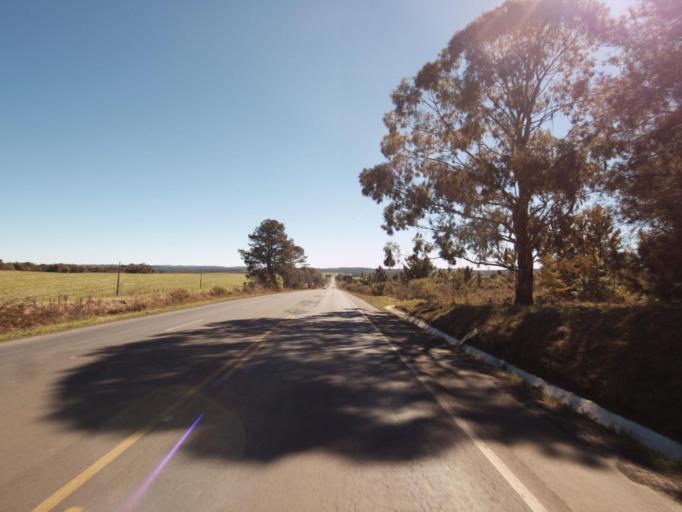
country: BR
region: Santa Catarina
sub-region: Concordia
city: Concordia
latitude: -26.9479
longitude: -51.8597
